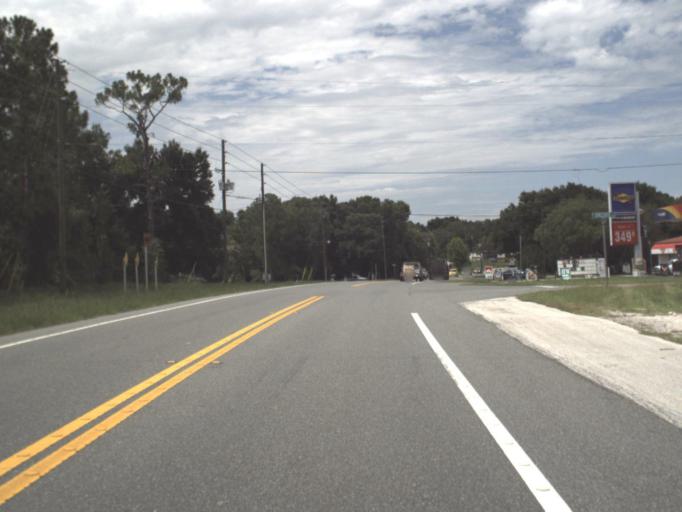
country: US
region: Florida
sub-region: Citrus County
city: Hernando
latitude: 28.9600
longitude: -82.3773
